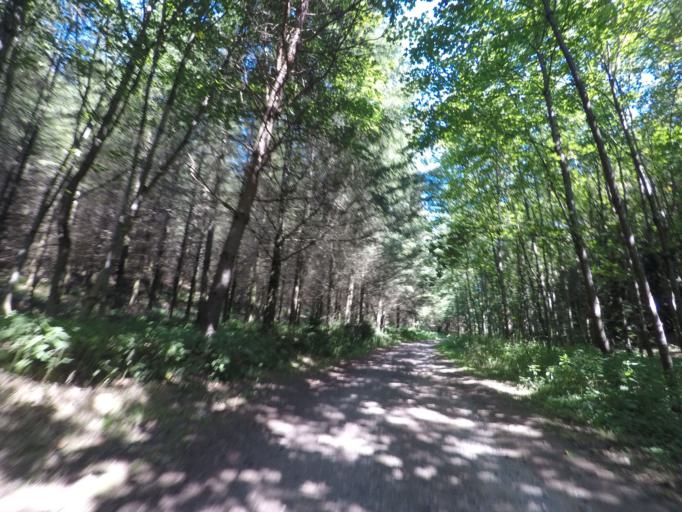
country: LU
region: Luxembourg
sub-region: Canton de Luxembourg
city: Strassen
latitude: 49.6328
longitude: 6.0900
